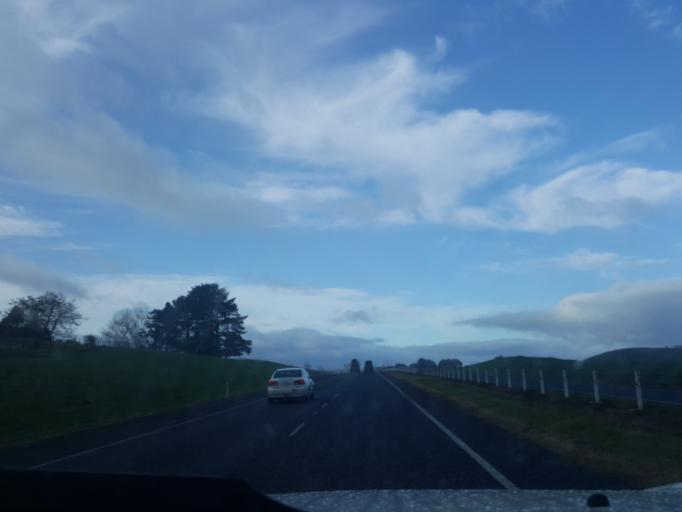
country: NZ
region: Waikato
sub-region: Waikato District
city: Ngaruawahia
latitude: -37.6647
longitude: 175.2067
